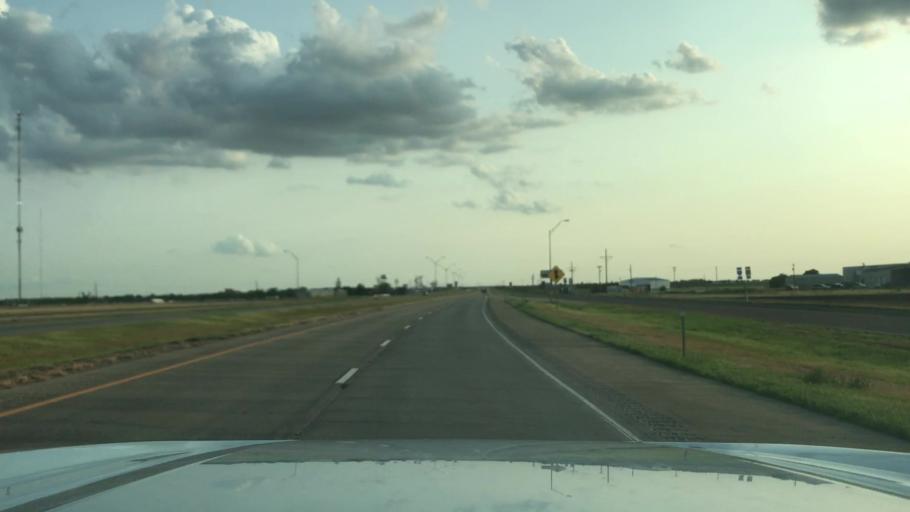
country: US
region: Texas
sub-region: Hale County
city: Seth Ward
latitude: 34.2313
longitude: -101.7116
